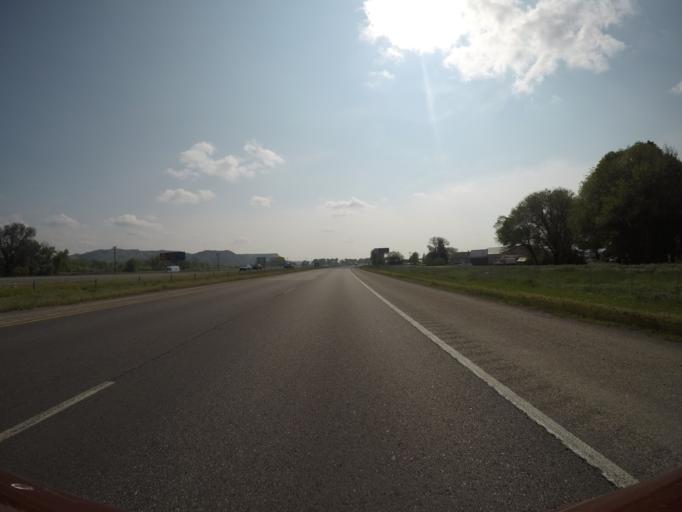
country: US
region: Montana
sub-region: Yellowstone County
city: Billings
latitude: 45.7561
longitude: -108.4968
